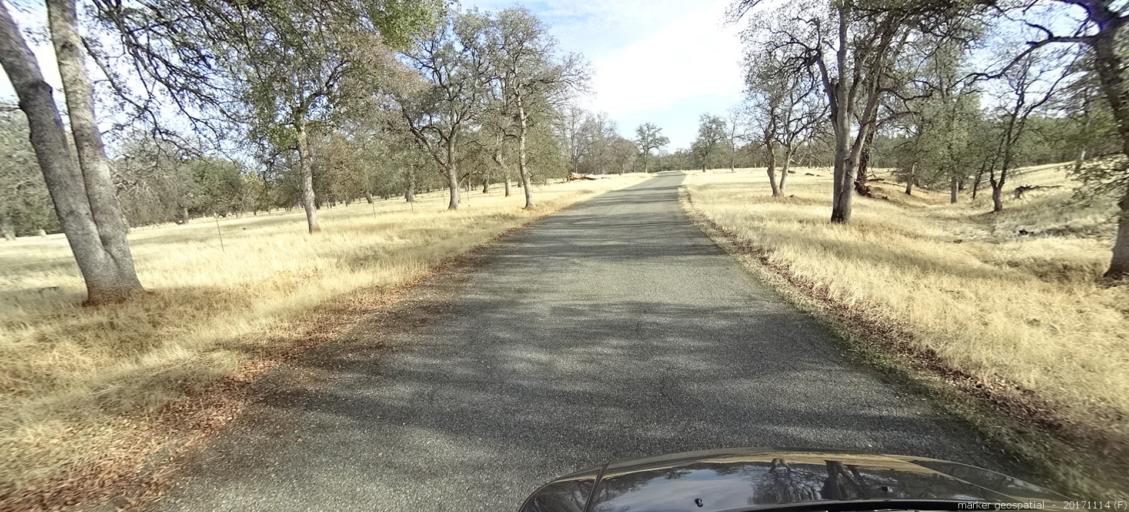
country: US
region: California
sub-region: Shasta County
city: Shasta
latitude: 40.3817
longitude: -122.5709
